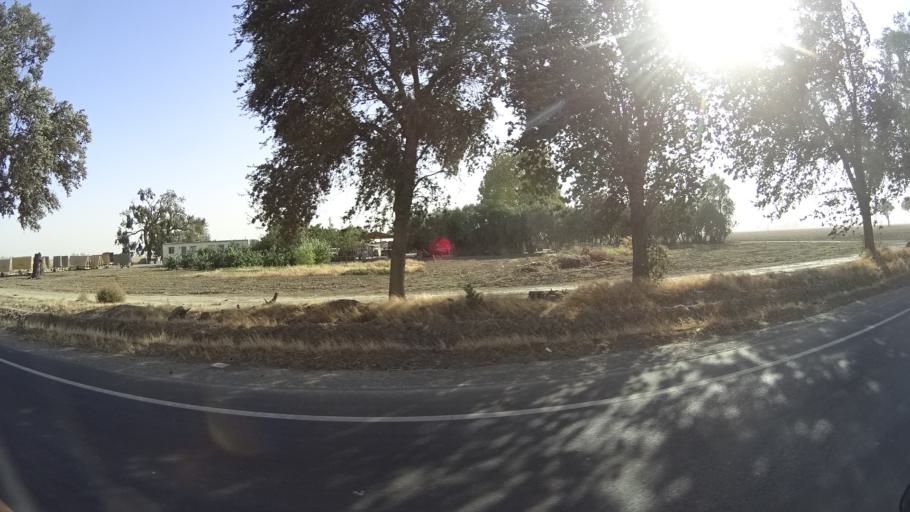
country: US
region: California
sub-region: Yolo County
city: Woodland
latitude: 38.7930
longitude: -121.7628
